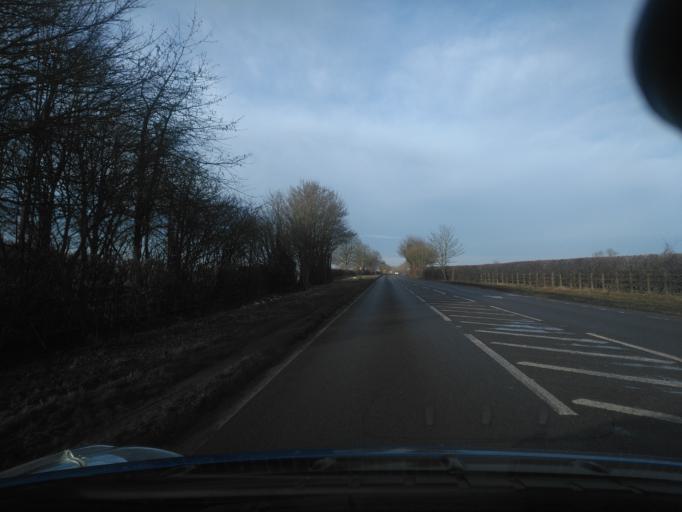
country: GB
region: England
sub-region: Oxfordshire
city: Woodstock
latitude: 51.8642
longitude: -1.3691
